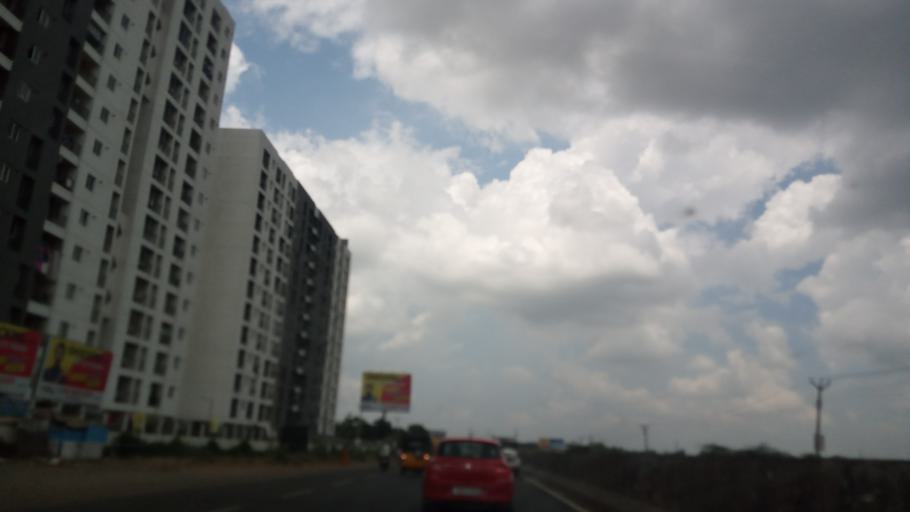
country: IN
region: Tamil Nadu
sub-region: Kancheepuram
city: Vandalur
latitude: 12.8951
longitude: 80.0550
